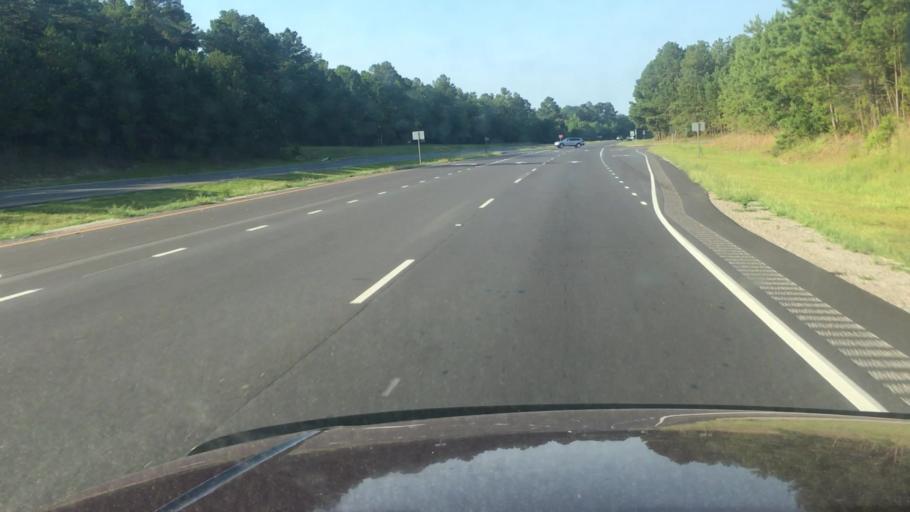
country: US
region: North Carolina
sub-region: Robeson County
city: Saint Pauls
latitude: 34.8561
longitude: -78.8500
